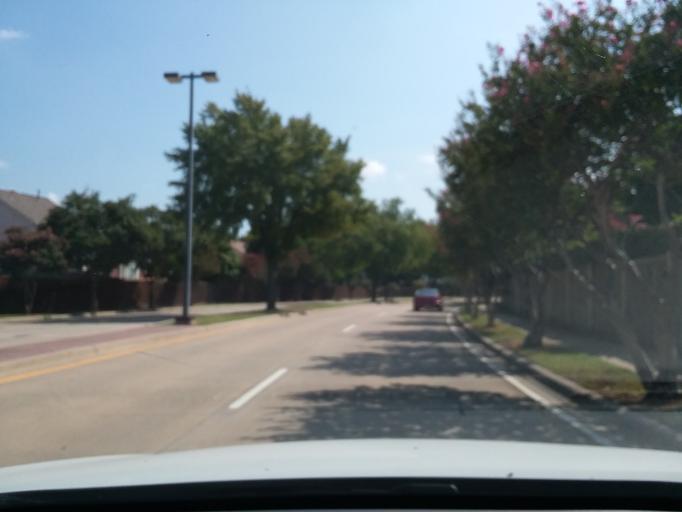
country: US
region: Texas
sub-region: Denton County
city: Flower Mound
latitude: 33.0198
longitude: -97.0533
